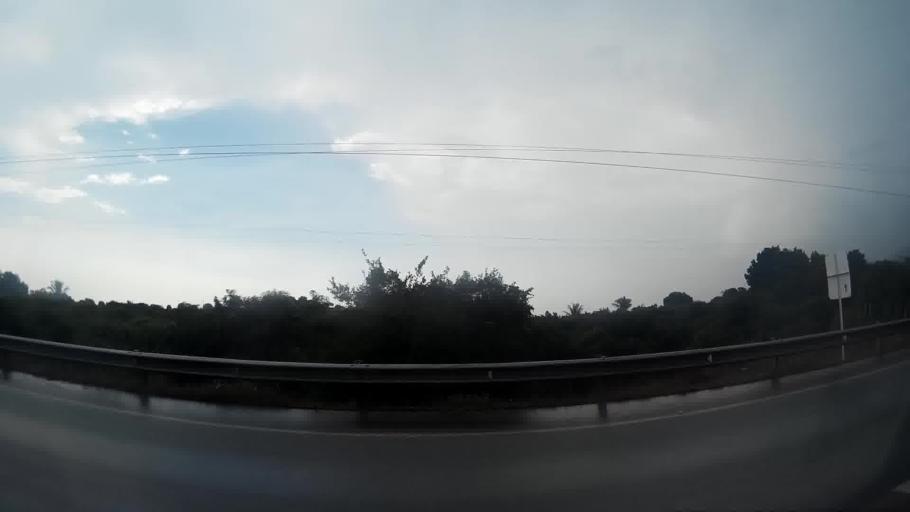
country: CO
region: Magdalena
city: Cienaga
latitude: 11.0194
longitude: -74.2115
